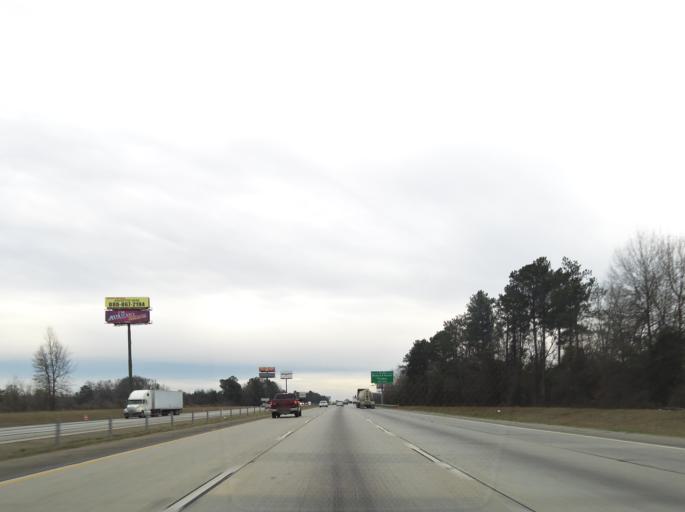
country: US
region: Georgia
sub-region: Peach County
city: Byron
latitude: 32.6078
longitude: -83.7430
